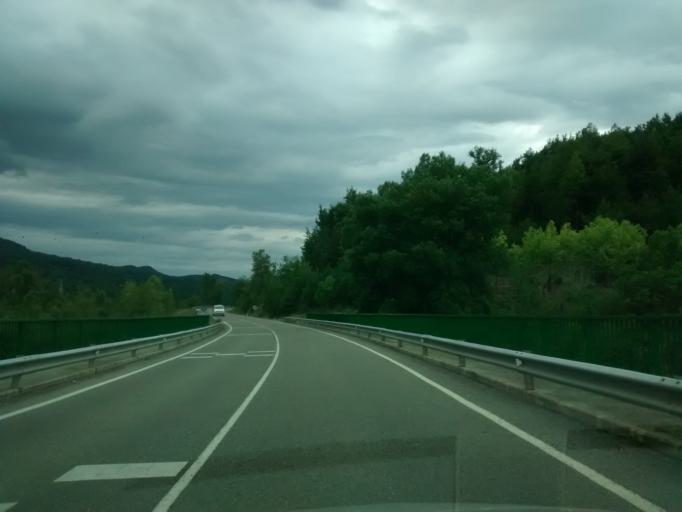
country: ES
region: Aragon
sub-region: Provincia de Huesca
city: Laspuna
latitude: 42.4970
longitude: 0.1444
